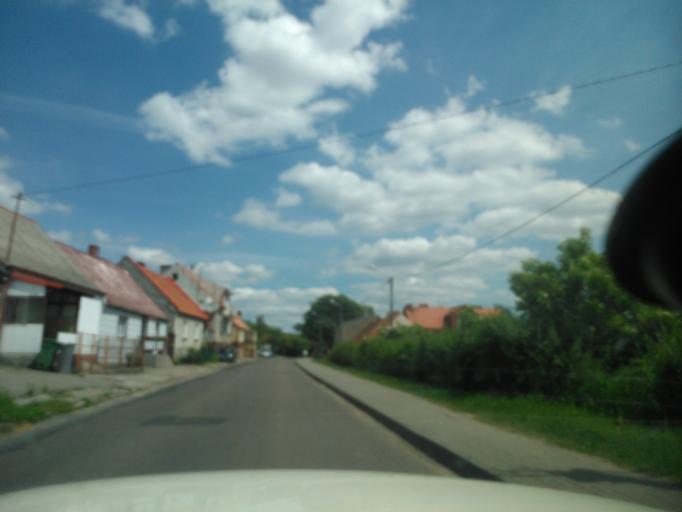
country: PL
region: Kujawsko-Pomorskie
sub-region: Powiat golubsko-dobrzynski
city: Golub-Dobrzyn
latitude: 53.1143
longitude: 19.0501
